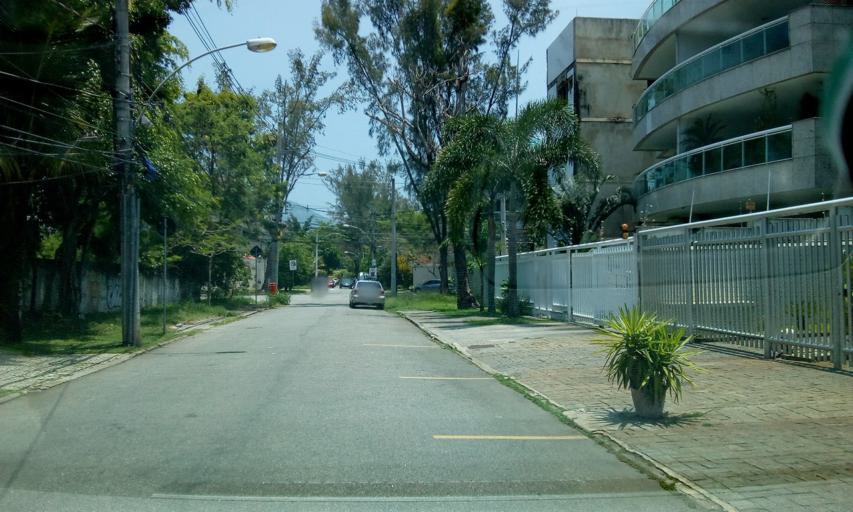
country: BR
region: Rio de Janeiro
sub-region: Nilopolis
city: Nilopolis
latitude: -23.0209
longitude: -43.4728
